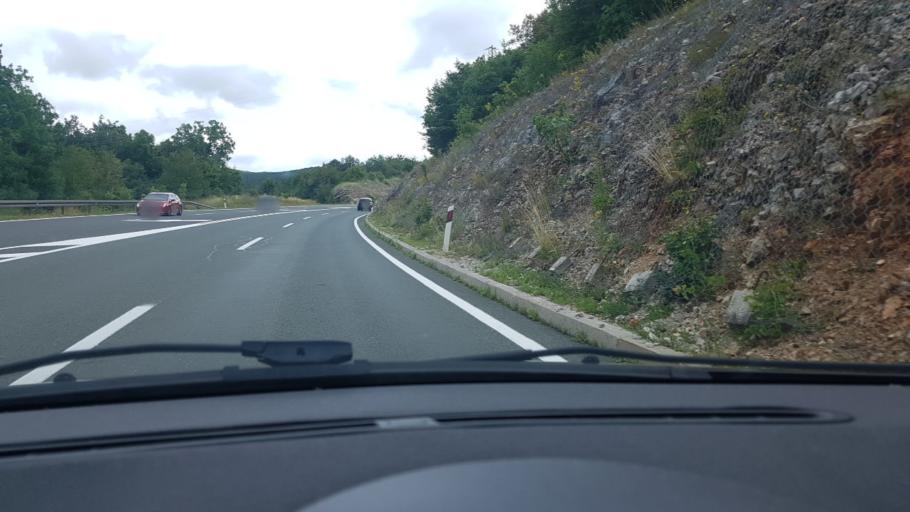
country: BA
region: Federation of Bosnia and Herzegovina
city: Bihac
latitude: 44.6787
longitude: 15.7262
